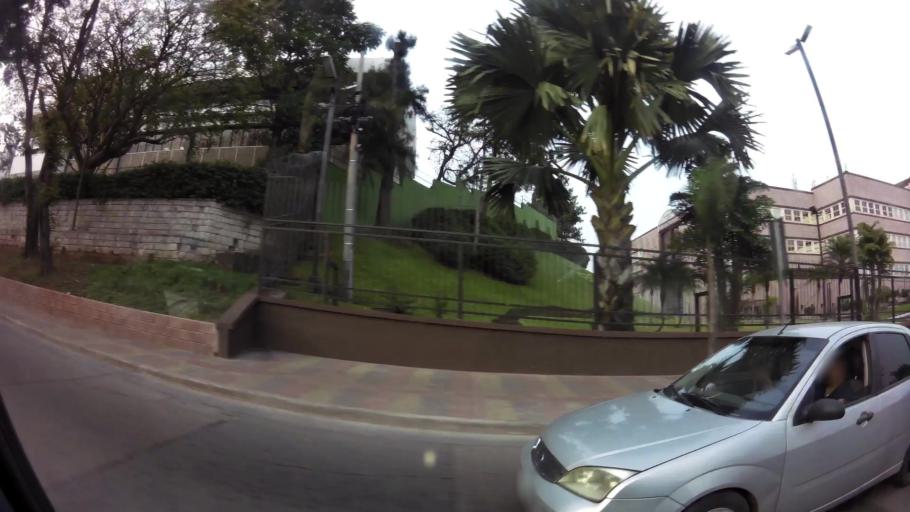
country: HN
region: Francisco Morazan
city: Tegucigalpa
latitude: 14.0867
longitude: -87.1930
